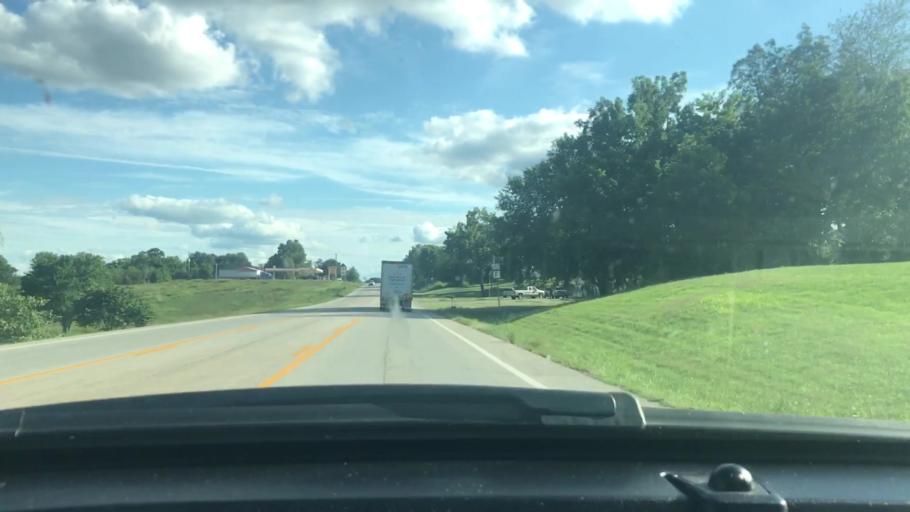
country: US
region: Missouri
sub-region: Oregon County
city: Thayer
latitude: 36.5980
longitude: -91.6440
